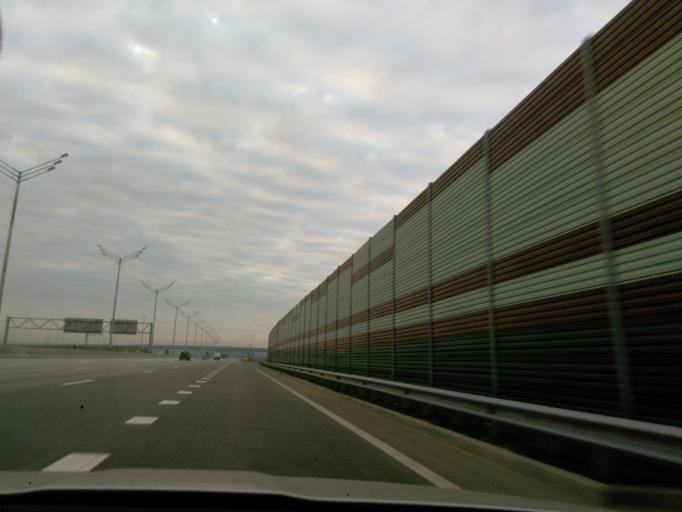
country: RU
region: Moskovskaya
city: Novopodrezkovo
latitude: 55.9591
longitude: 37.3612
